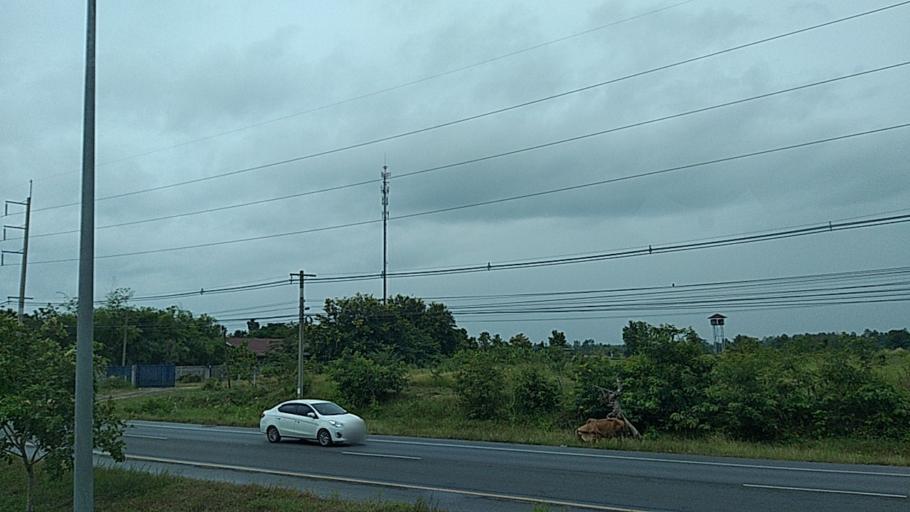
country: TH
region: Maha Sarakham
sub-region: Amphoe Borabue
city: Borabue
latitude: 16.0618
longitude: 103.1396
